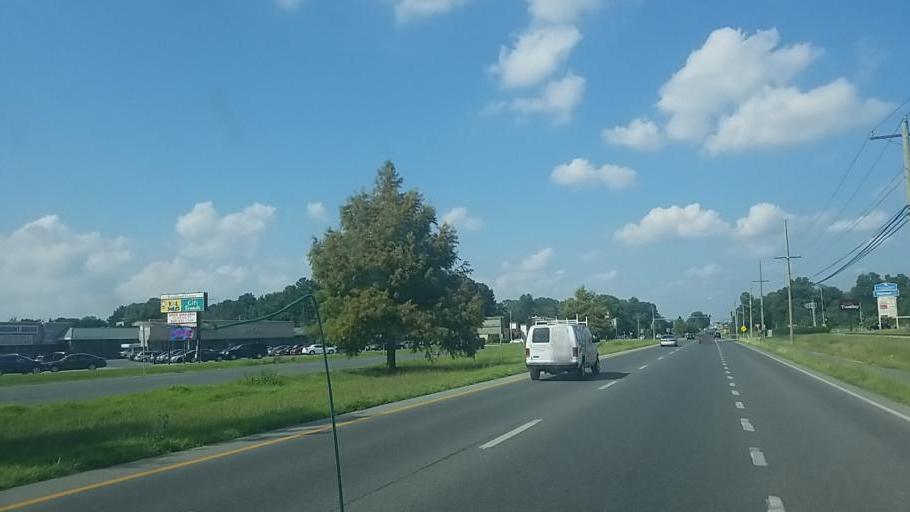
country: US
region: Maryland
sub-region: Wicomico County
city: Fruitland
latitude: 38.3300
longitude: -75.6130
